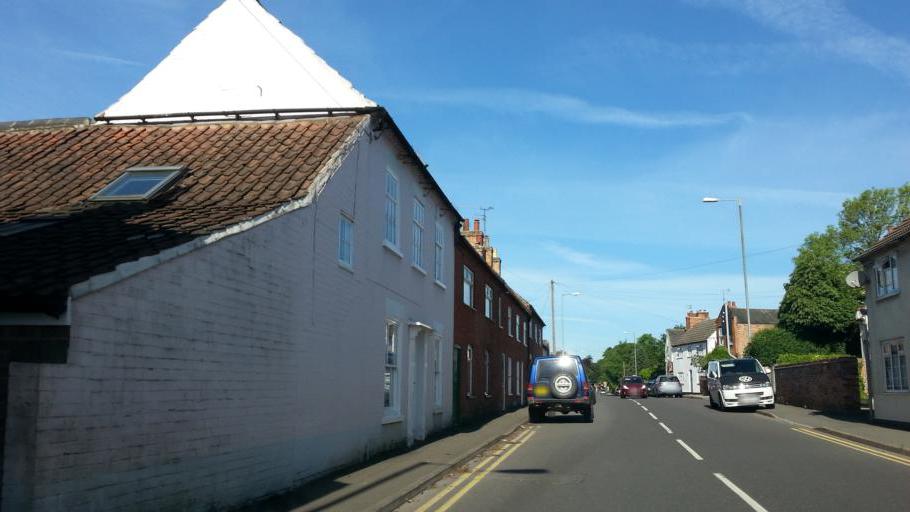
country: GB
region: England
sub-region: Nottinghamshire
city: Southwell
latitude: 53.0750
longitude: -0.9619
